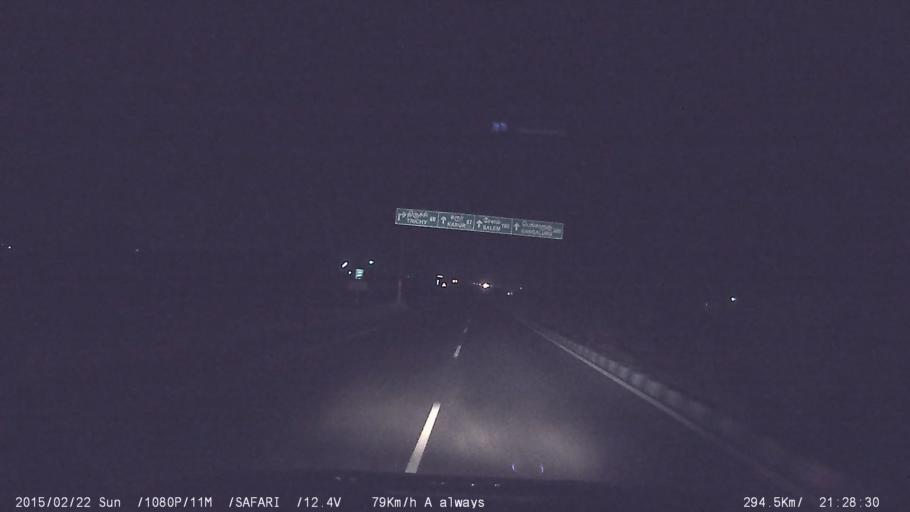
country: IN
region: Tamil Nadu
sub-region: Karur
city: Karur
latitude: 10.9257
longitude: 78.0497
